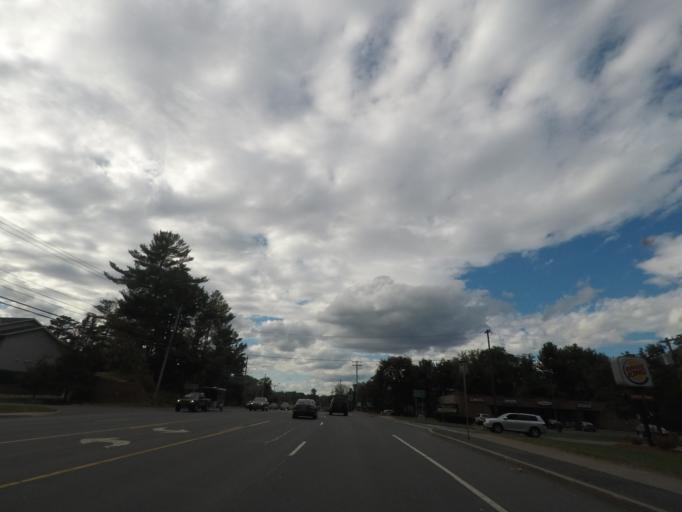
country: US
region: New York
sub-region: Albany County
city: Westmere
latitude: 42.6963
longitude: -73.8831
